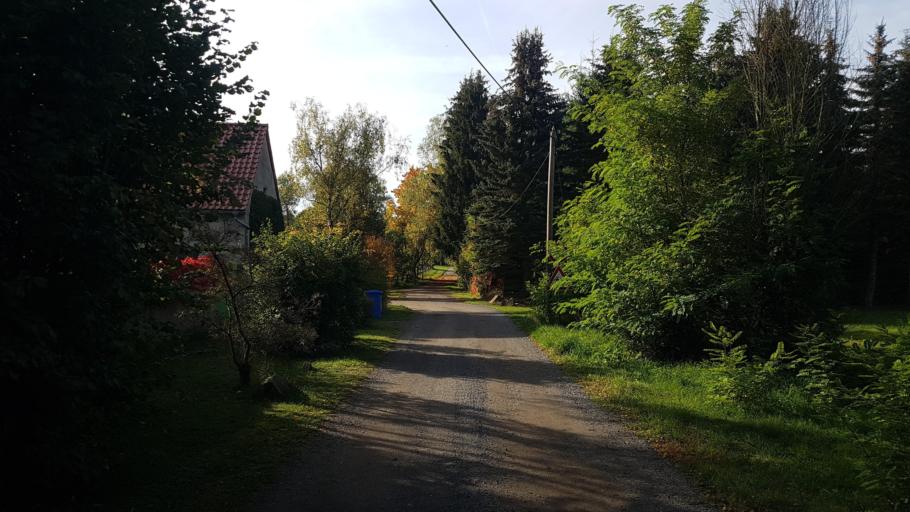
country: DE
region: Brandenburg
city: Hohenbucko
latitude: 51.8196
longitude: 13.5300
